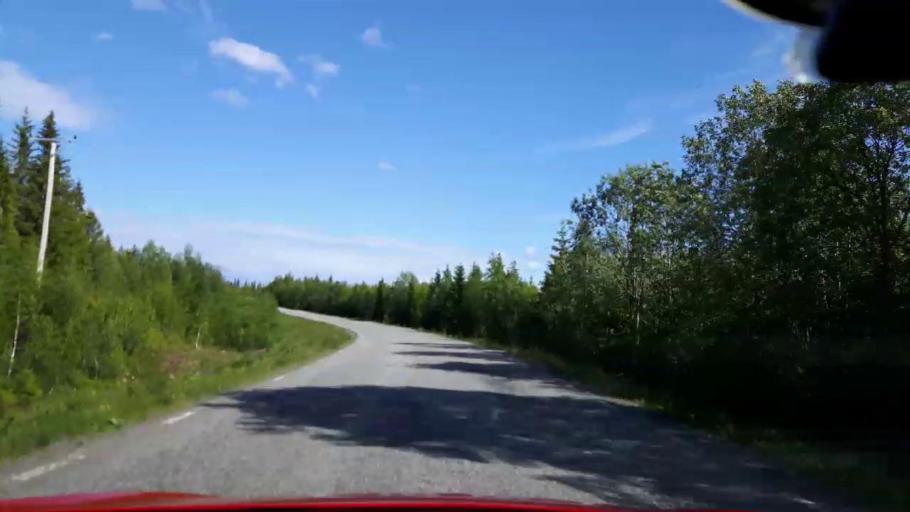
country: SE
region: Jaemtland
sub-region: Krokoms Kommun
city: Krokom
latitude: 63.6912
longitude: 14.2200
